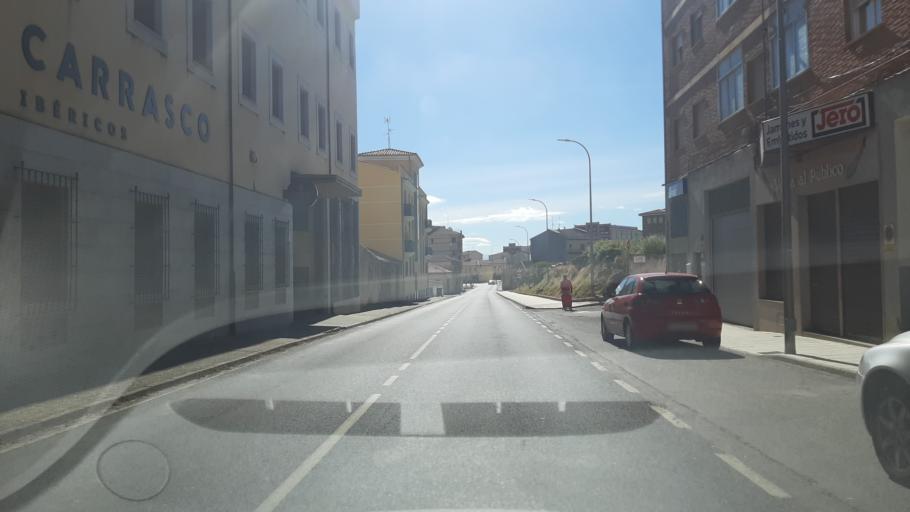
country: ES
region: Castille and Leon
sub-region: Provincia de Salamanca
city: Guijuelo
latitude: 40.5548
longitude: -5.6712
